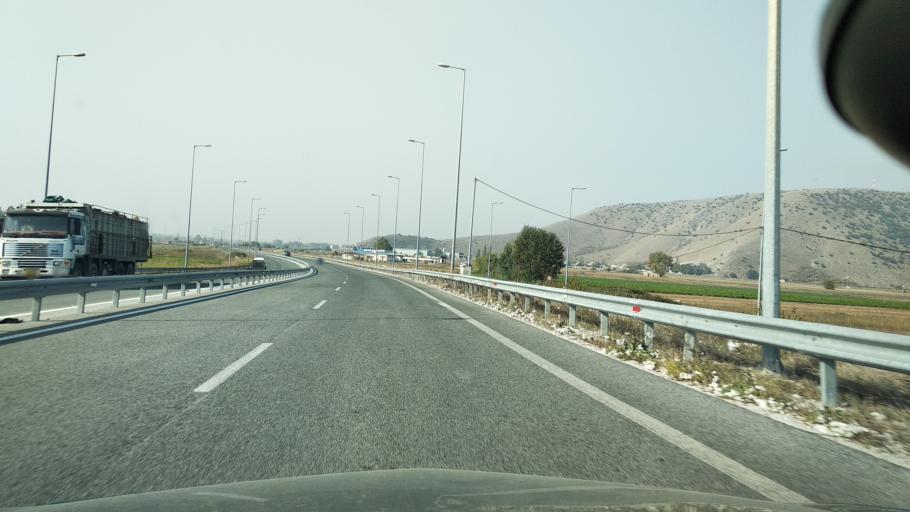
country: GR
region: Thessaly
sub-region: Trikala
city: Oichalia
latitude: 39.5700
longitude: 21.9841
